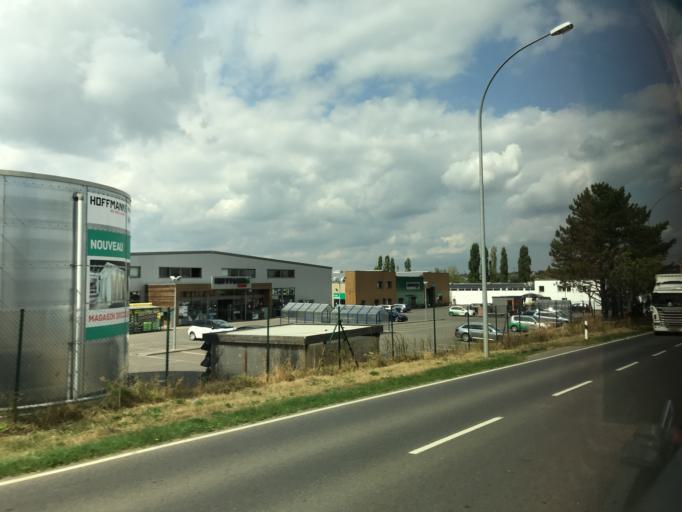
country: LU
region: Luxembourg
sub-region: Canton de Luxembourg
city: Alzingen
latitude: 49.5601
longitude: 6.1664
